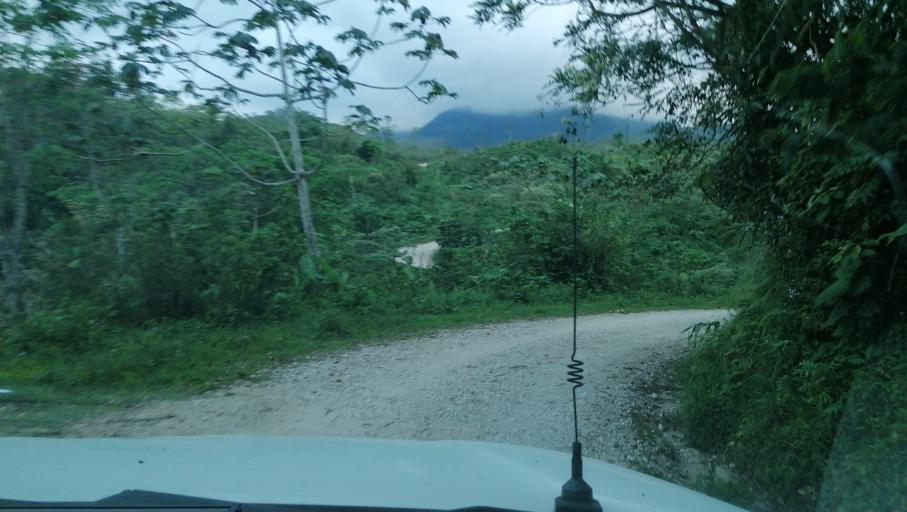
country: MX
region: Chiapas
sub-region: Francisco Leon
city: San Miguel la Sardina
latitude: 17.2931
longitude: -93.2685
